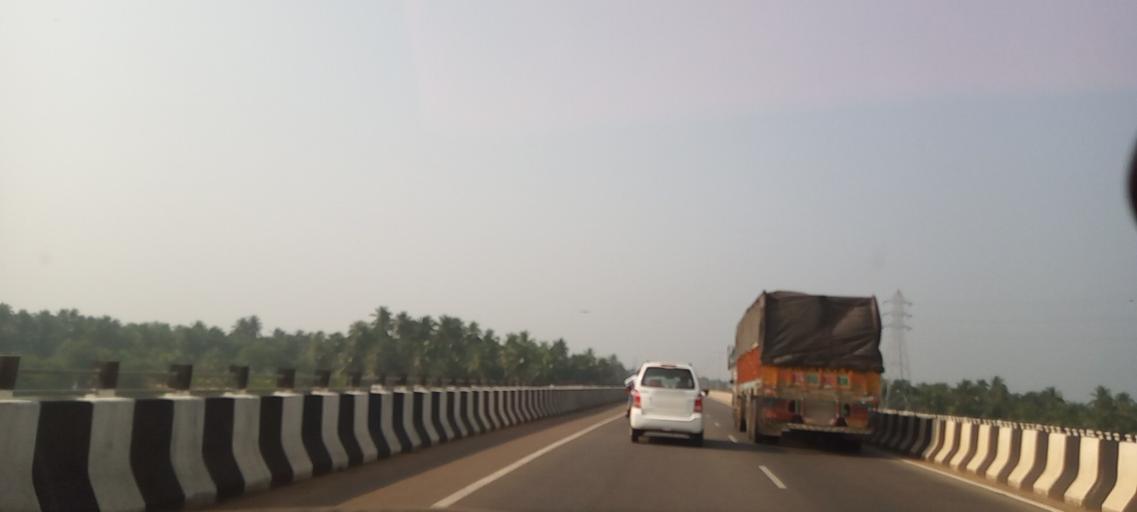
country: IN
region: Karnataka
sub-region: Udupi
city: Coondapoor
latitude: 13.6478
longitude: 74.7046
